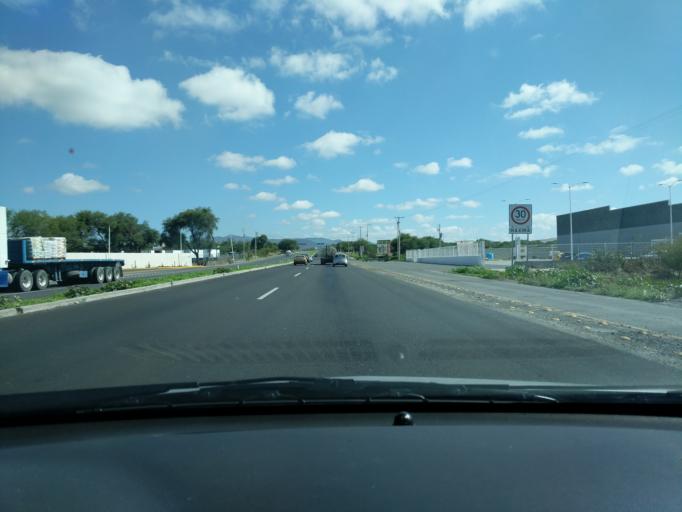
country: MX
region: Queretaro
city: Tlacote el Bajo
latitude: 20.6443
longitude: -100.5011
